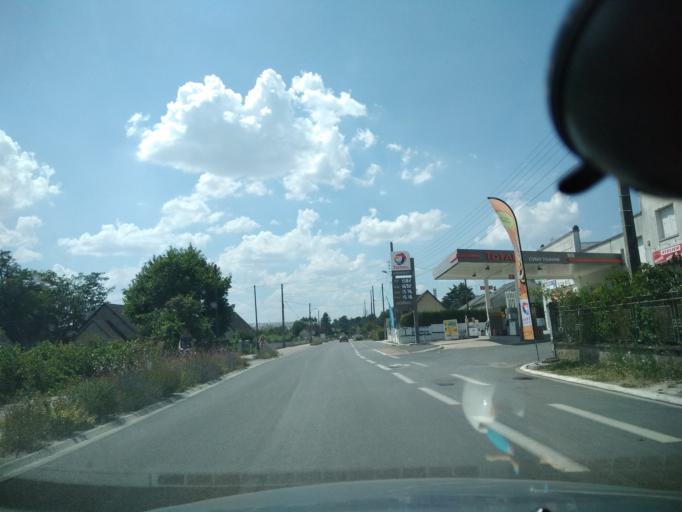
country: FR
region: Centre
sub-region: Departement d'Indre-et-Loire
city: Civray-de-Touraine
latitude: 47.3323
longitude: 1.0614
